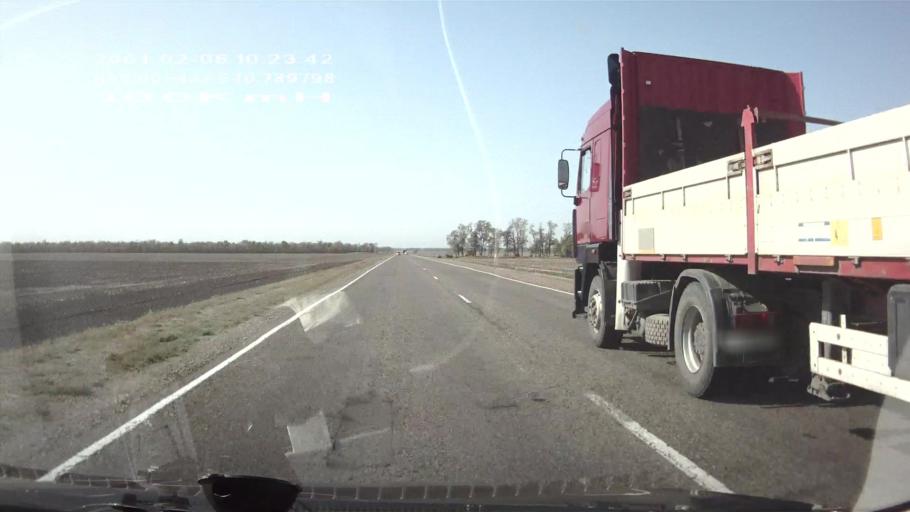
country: RU
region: Krasnodarskiy
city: Novopokrovskaya
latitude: 46.0054
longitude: 40.7899
